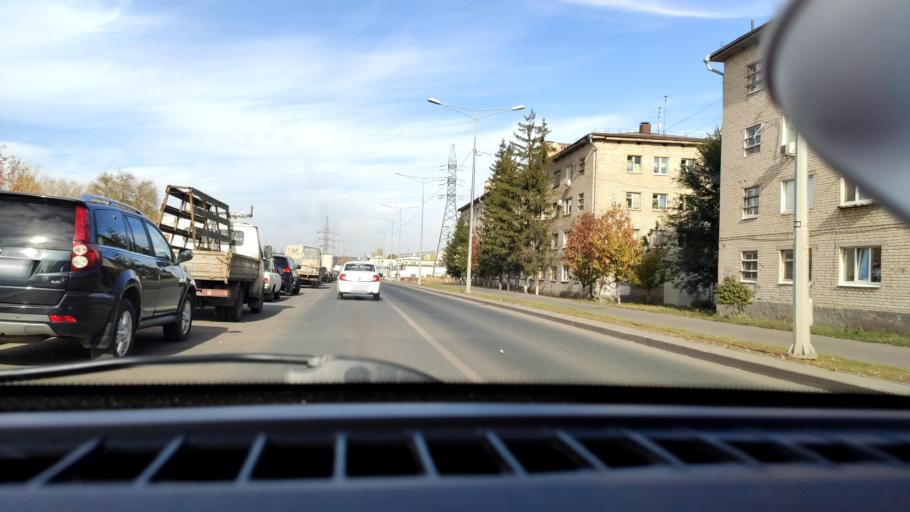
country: RU
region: Samara
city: Petra-Dubrava
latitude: 53.3009
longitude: 50.2891
